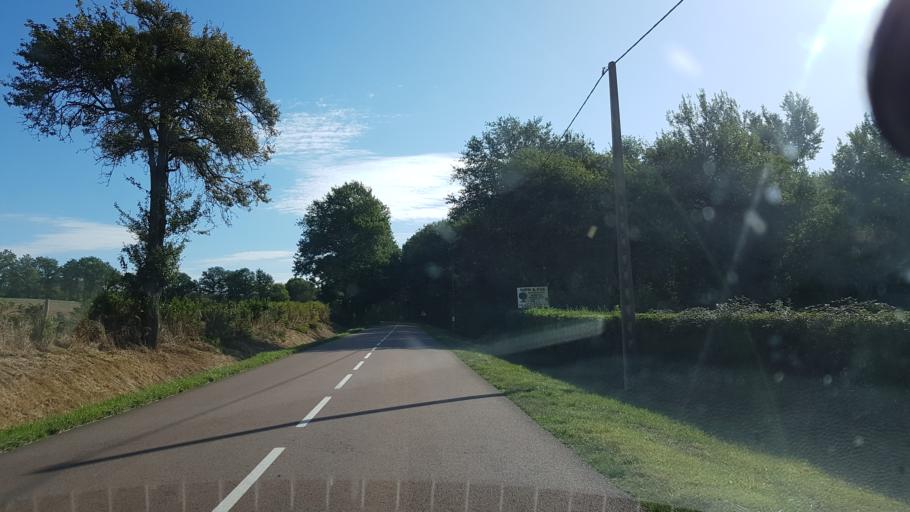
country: FR
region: Bourgogne
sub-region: Departement de la Nievre
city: Saint-Amand-en-Puisaye
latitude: 47.5371
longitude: 3.0184
